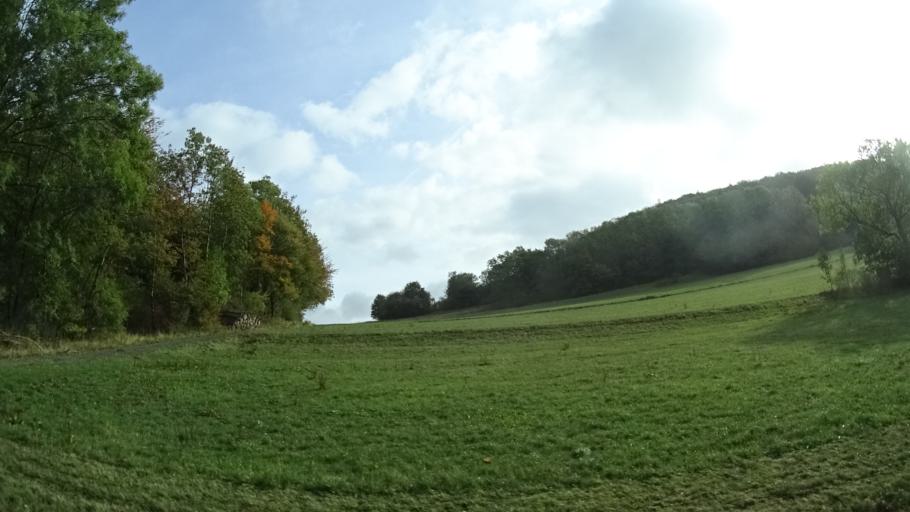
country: DE
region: Hesse
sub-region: Regierungsbezirk Kassel
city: Hilders
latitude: 50.5809
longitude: 10.0148
